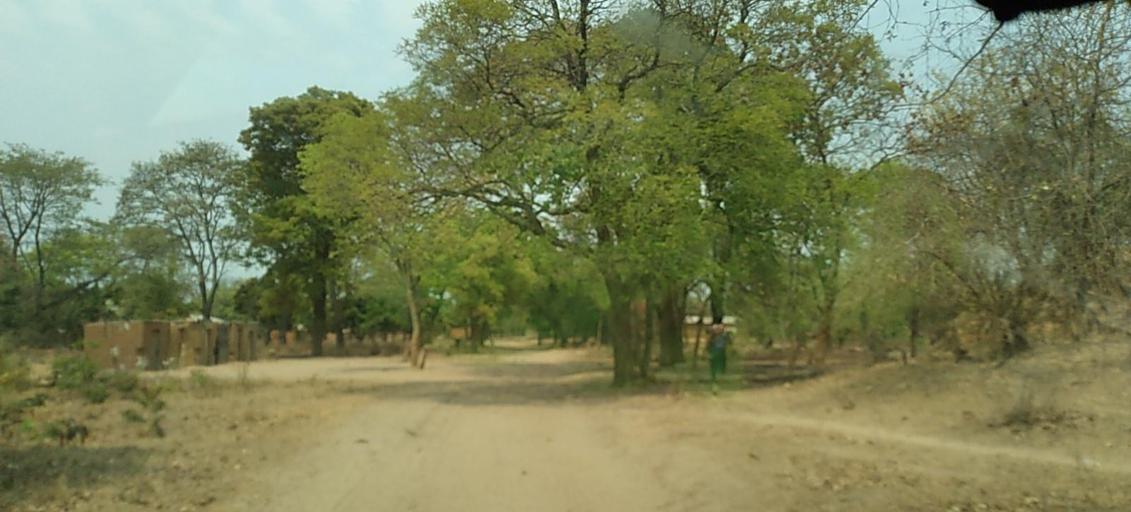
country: ZM
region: North-Western
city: Kabompo
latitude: -13.5633
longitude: 24.4450
